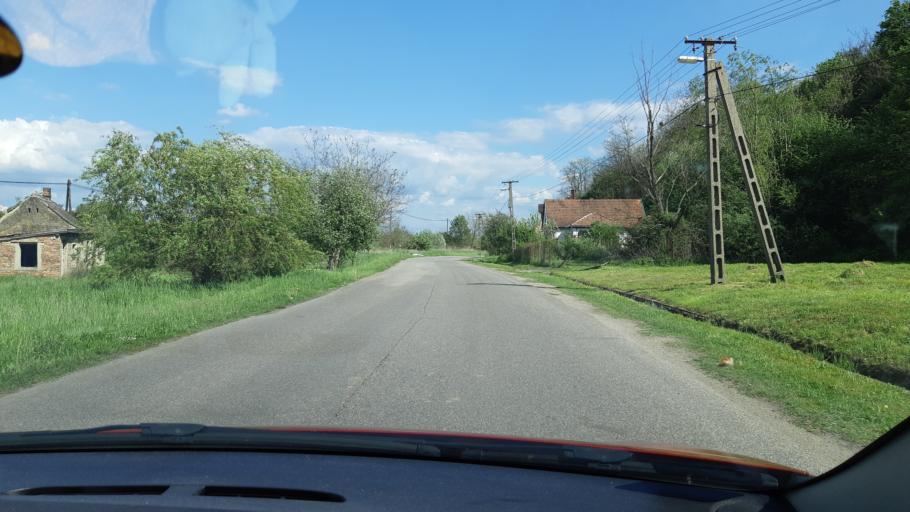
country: HU
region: Somogy
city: Kaposvar
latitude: 46.3634
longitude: 17.7619
